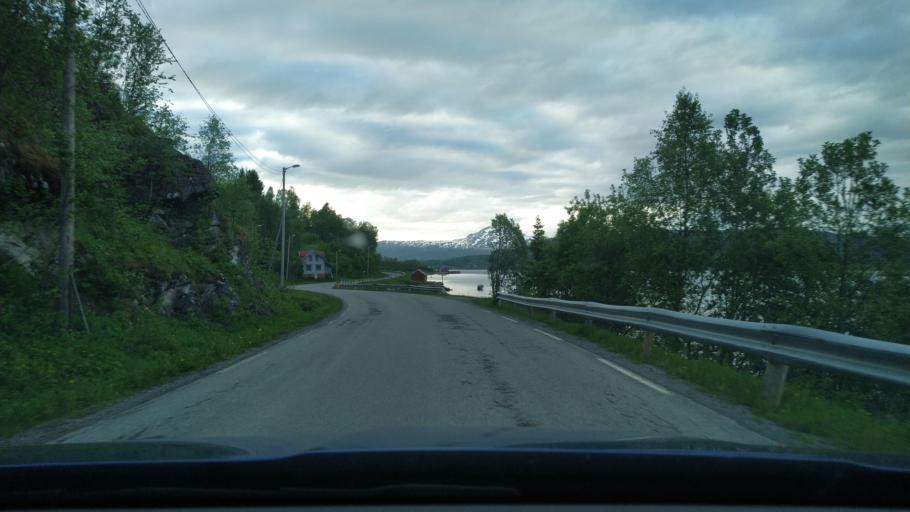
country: NO
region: Troms
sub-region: Sorreisa
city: Sorreisa
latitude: 69.1390
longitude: 18.0579
